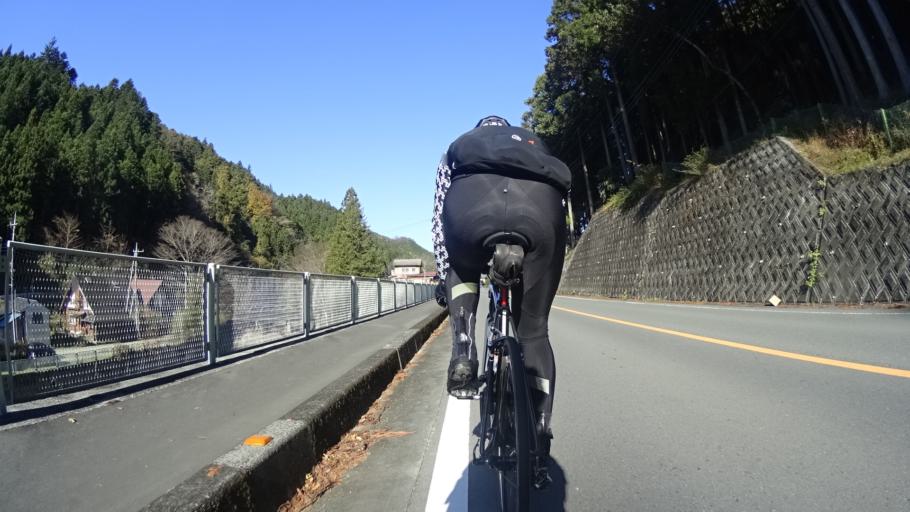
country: JP
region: Tokyo
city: Ome
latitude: 35.8735
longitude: 139.1873
